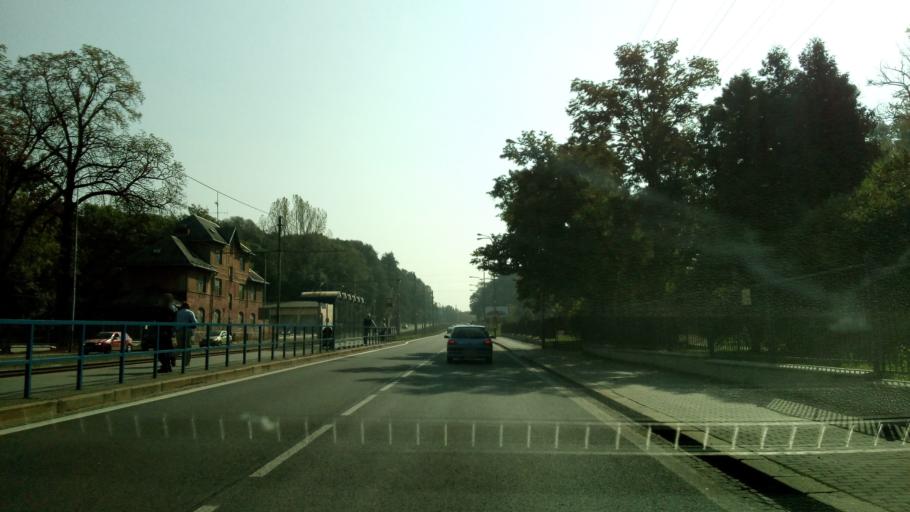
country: CZ
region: Moravskoslezsky
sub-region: Okres Ostrava-Mesto
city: Ostrava
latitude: 49.8238
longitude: 18.2347
